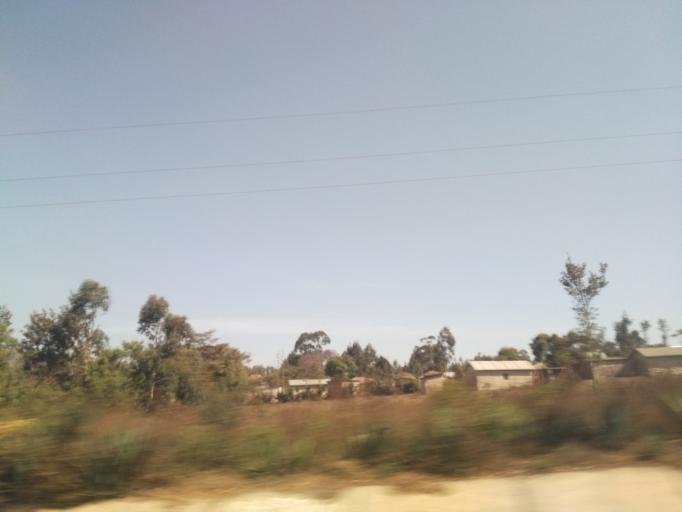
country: TZ
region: Arusha
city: Arusha
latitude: -3.2130
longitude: 36.6152
